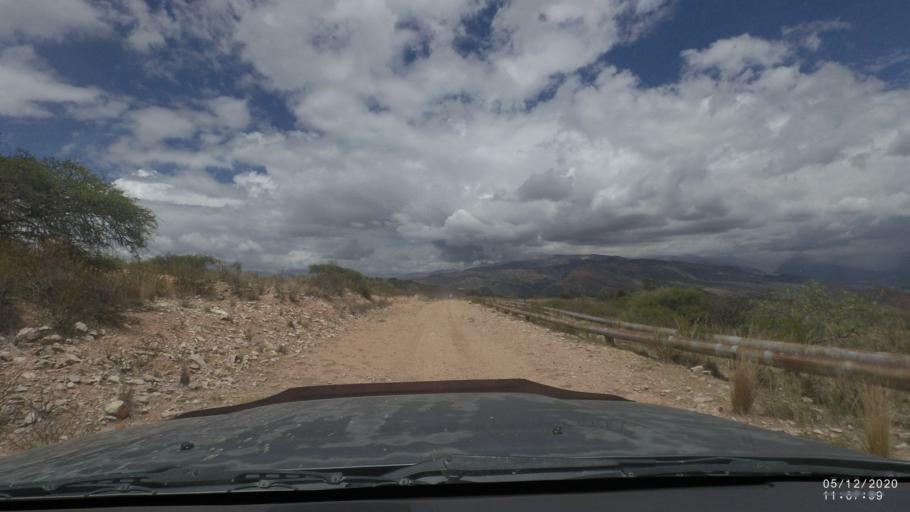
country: BO
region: Cochabamba
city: Sipe Sipe
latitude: -17.5521
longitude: -66.3114
